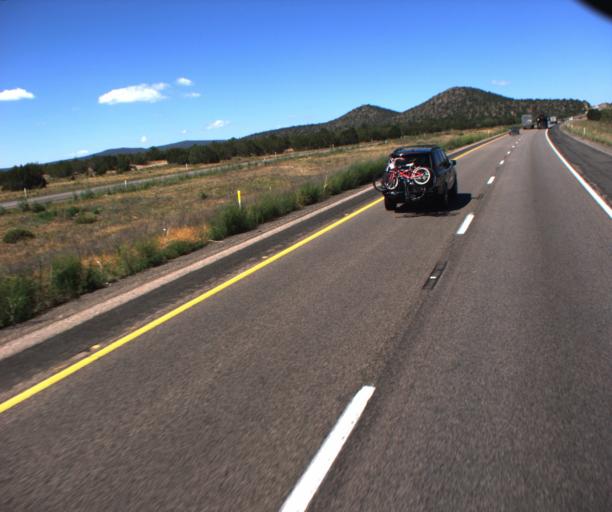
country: US
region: Arizona
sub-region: Mohave County
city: Peach Springs
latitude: 35.3035
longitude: -113.0007
